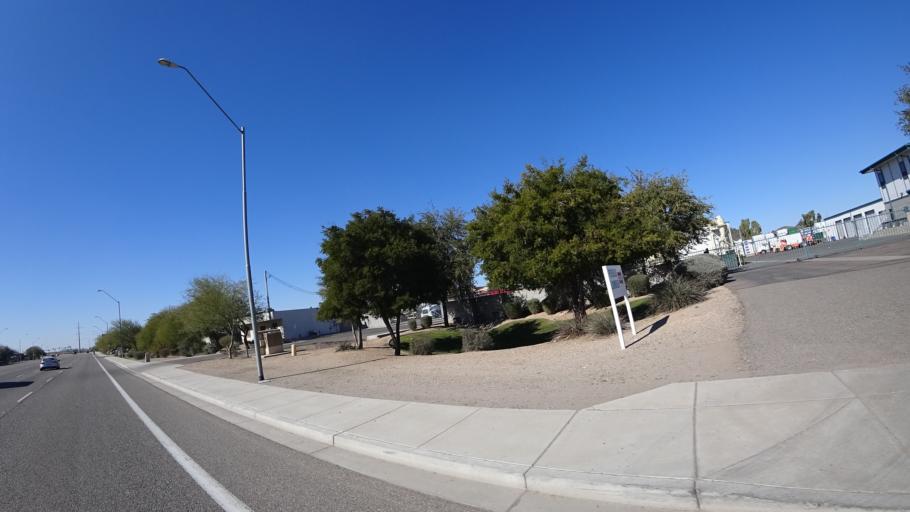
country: US
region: Arizona
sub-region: Maricopa County
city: Cave Creek
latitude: 33.6879
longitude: -112.0439
